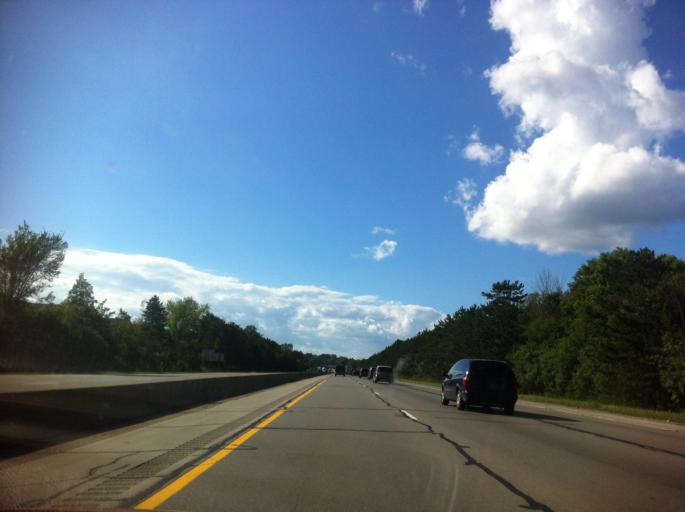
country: US
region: Michigan
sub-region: Washtenaw County
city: Ann Arbor
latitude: 42.2388
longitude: -83.7541
